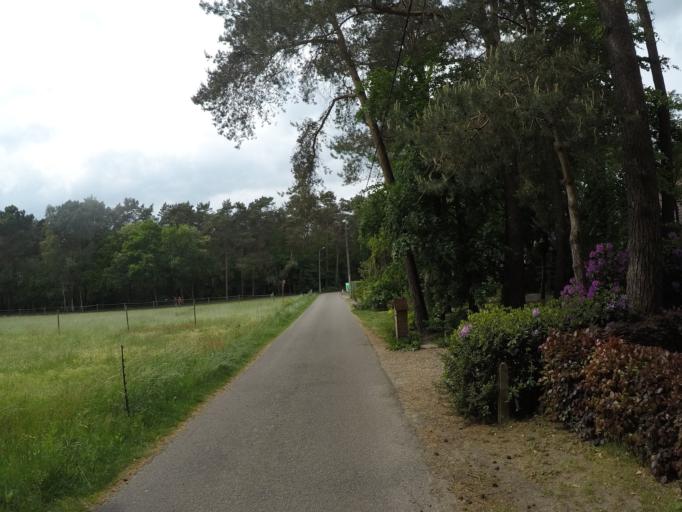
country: BE
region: Flanders
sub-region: Provincie Antwerpen
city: Zoersel
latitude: 51.2761
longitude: 4.6981
